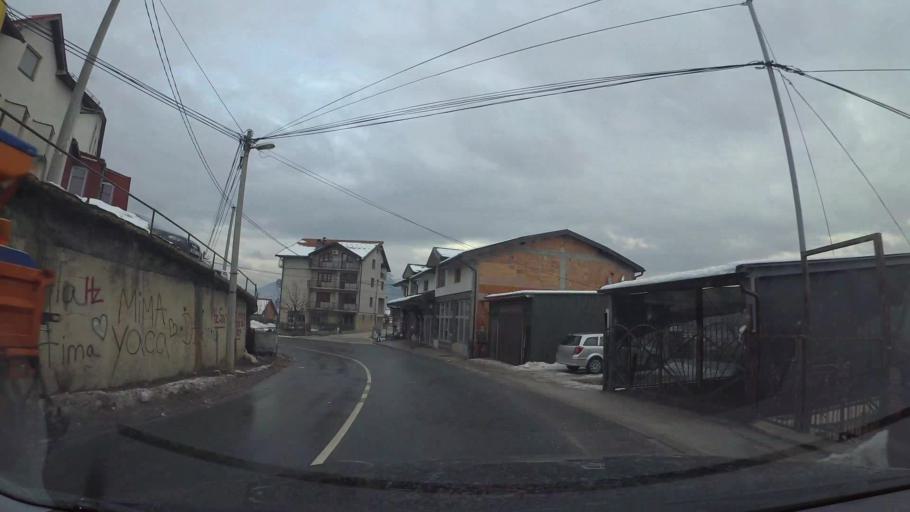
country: BA
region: Federation of Bosnia and Herzegovina
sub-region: Kanton Sarajevo
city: Sarajevo
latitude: 43.8578
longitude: 18.3572
